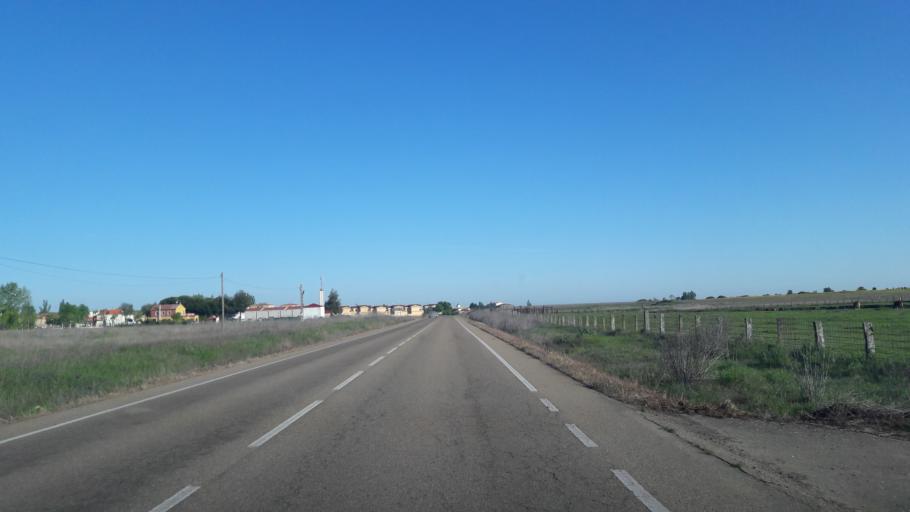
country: ES
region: Castille and Leon
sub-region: Provincia de Salamanca
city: La Fuente de San Esteban
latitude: 40.7963
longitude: -6.2491
